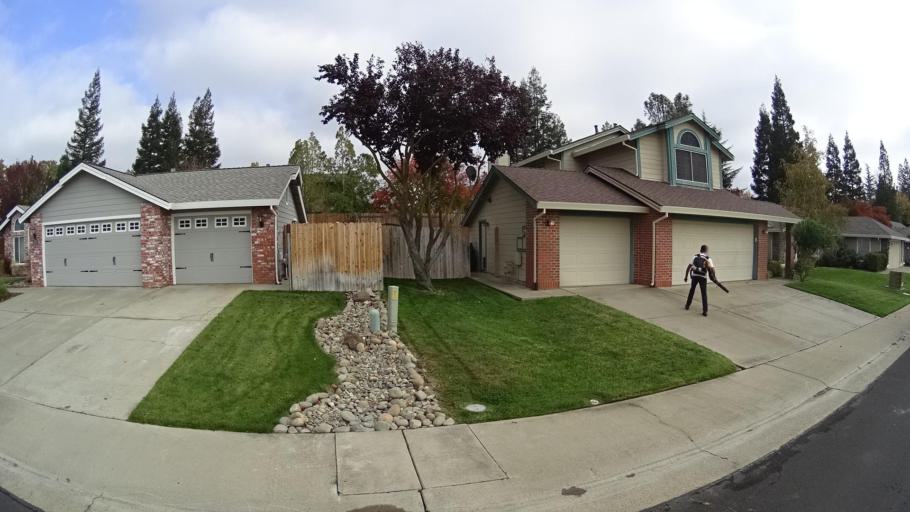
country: US
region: California
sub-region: Sacramento County
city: Elk Grove
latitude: 38.4228
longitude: -121.3601
